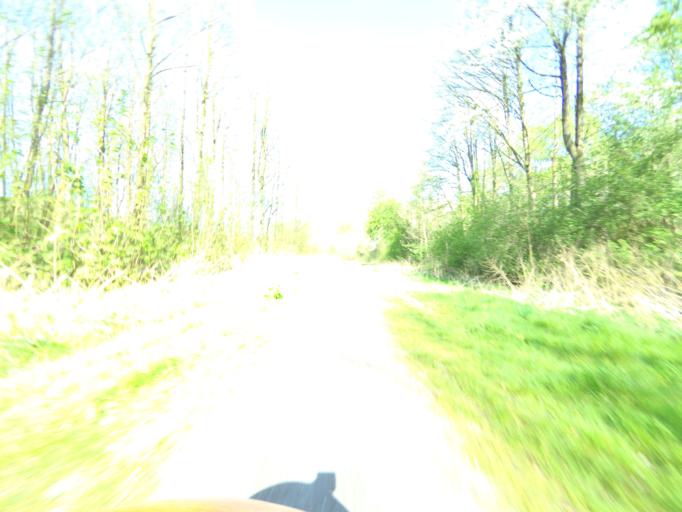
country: NL
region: Flevoland
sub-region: Gemeente Lelystad
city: Lelystad
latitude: 52.4457
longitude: 5.5594
